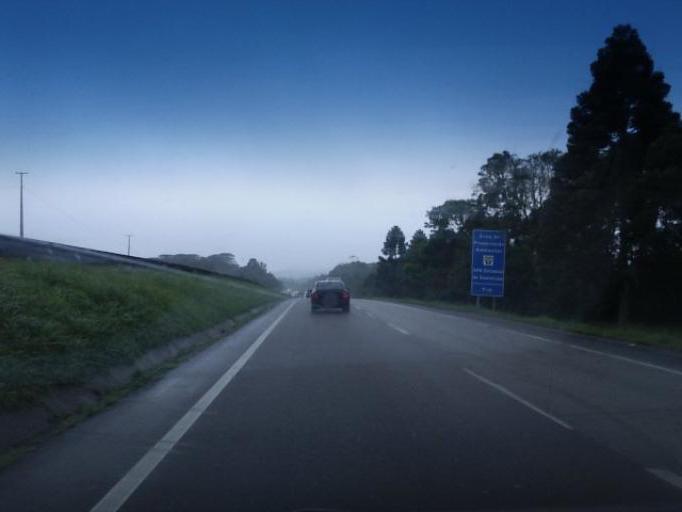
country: BR
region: Parana
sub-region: Sao Jose Dos Pinhais
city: Sao Jose dos Pinhais
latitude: -25.7906
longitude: -49.1257
